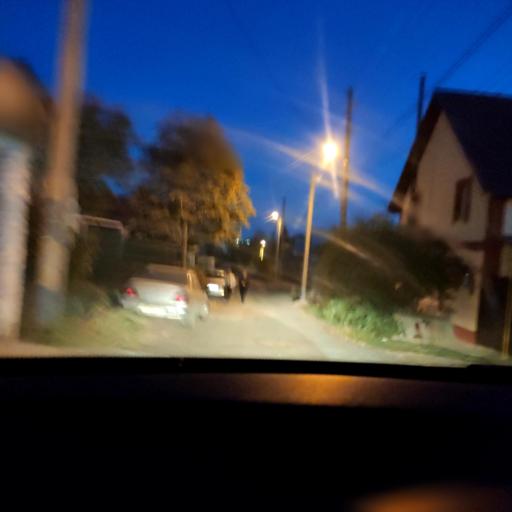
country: RU
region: Samara
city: Samara
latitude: 53.1769
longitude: 50.1774
